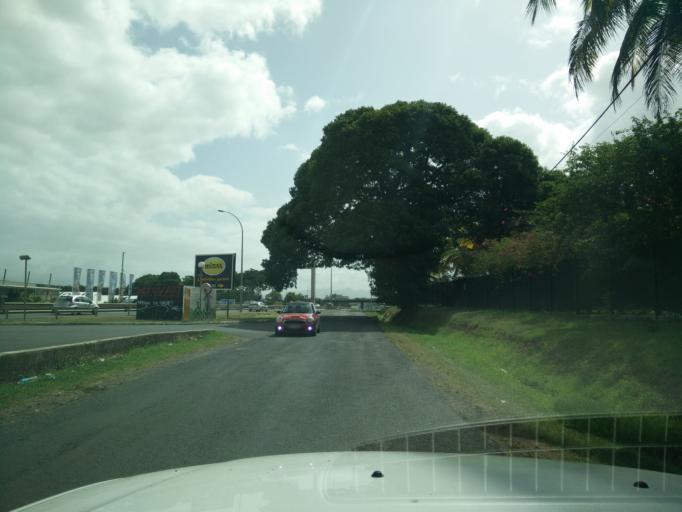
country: GP
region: Guadeloupe
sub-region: Guadeloupe
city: Baie-Mahault
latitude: 16.2546
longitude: -61.5681
